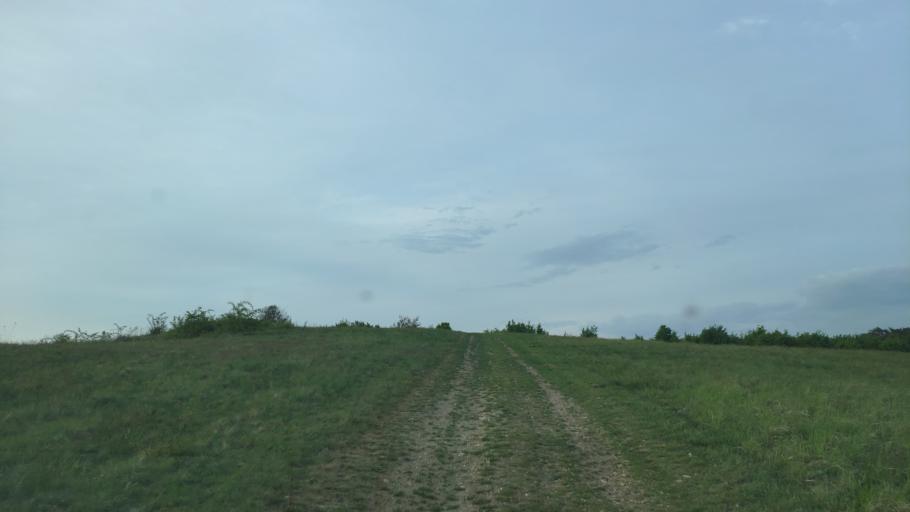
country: SK
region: Kosicky
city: Kosice
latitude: 48.7213
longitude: 21.3603
